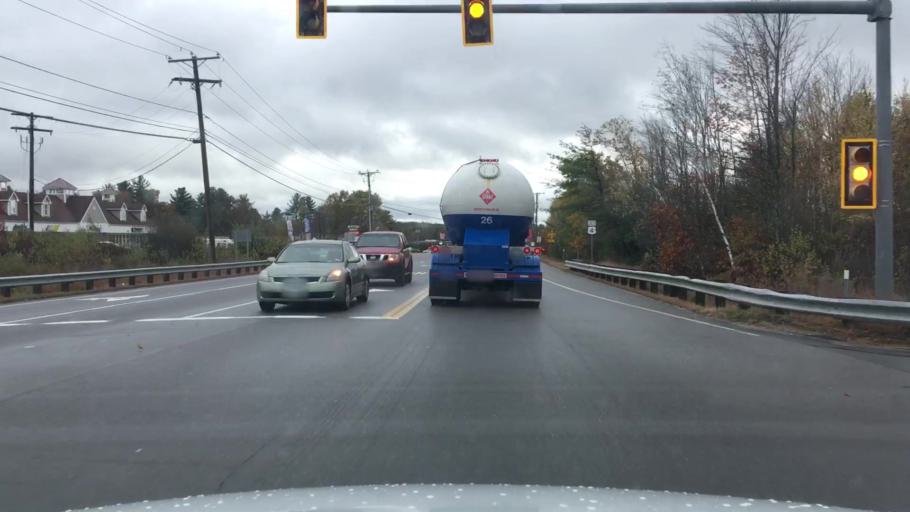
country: US
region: New Hampshire
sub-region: Strafford County
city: Lee
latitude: 43.1535
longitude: -71.0055
